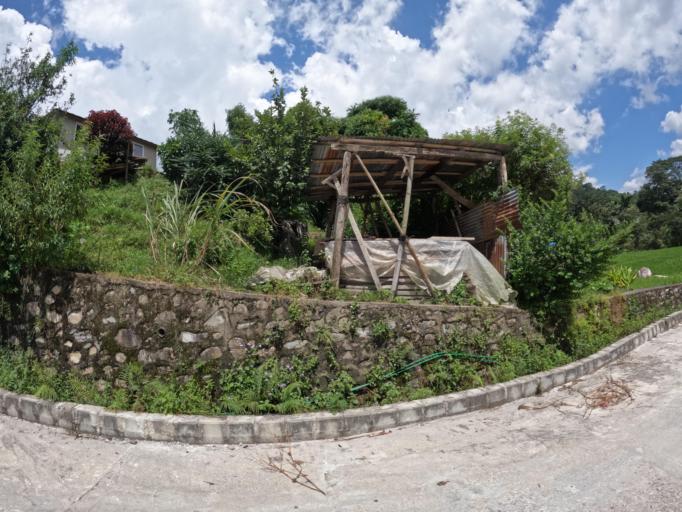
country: NP
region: Central Region
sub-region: Bagmati Zone
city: Kathmandu
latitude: 27.7843
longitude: 85.3276
